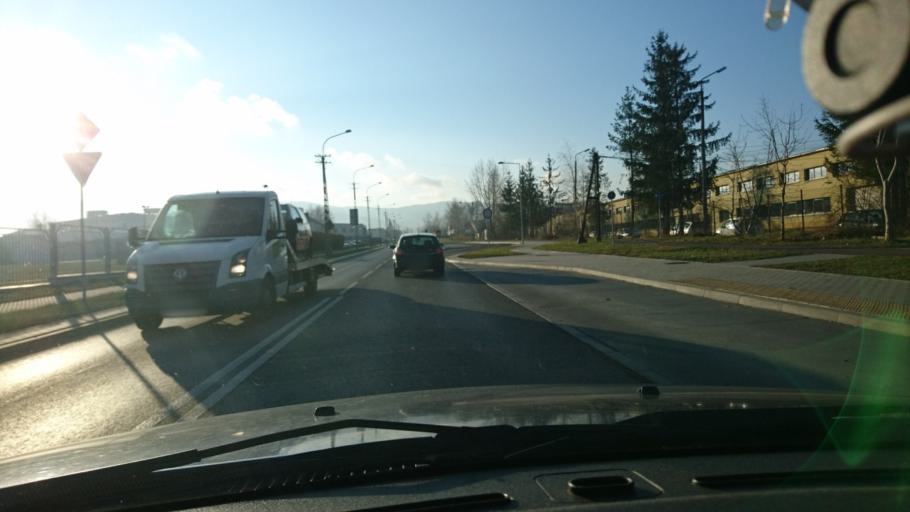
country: PL
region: Silesian Voivodeship
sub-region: Powiat bielski
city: Mazancowice
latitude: 49.8212
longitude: 18.9754
